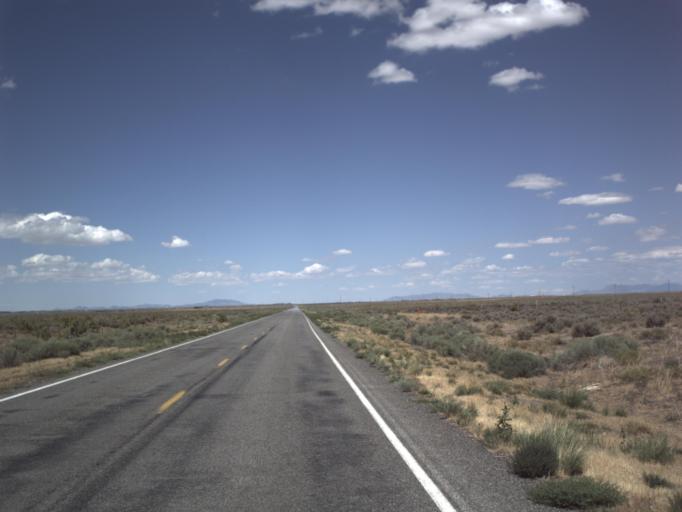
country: US
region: Utah
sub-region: Millard County
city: Delta
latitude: 39.2671
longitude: -112.4519
